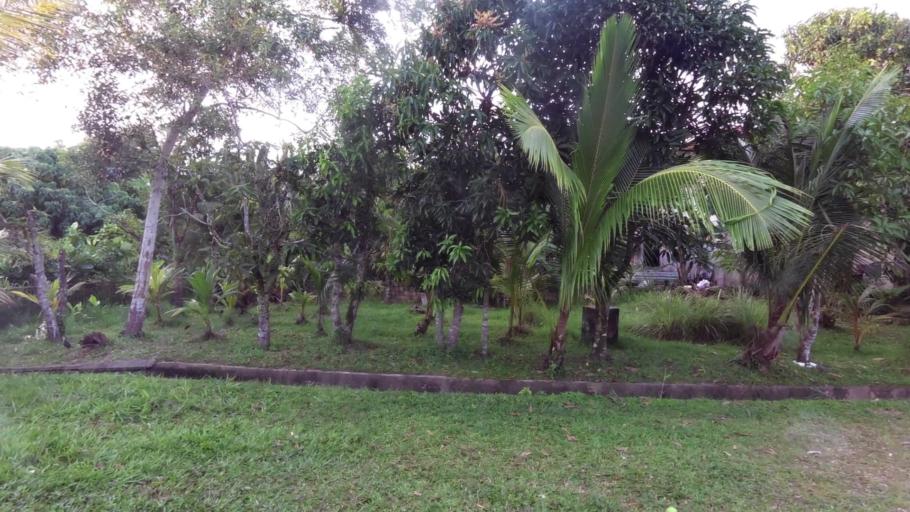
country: BN
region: Brunei and Muara
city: Bandar Seri Begawan
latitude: 4.9295
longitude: 114.8863
